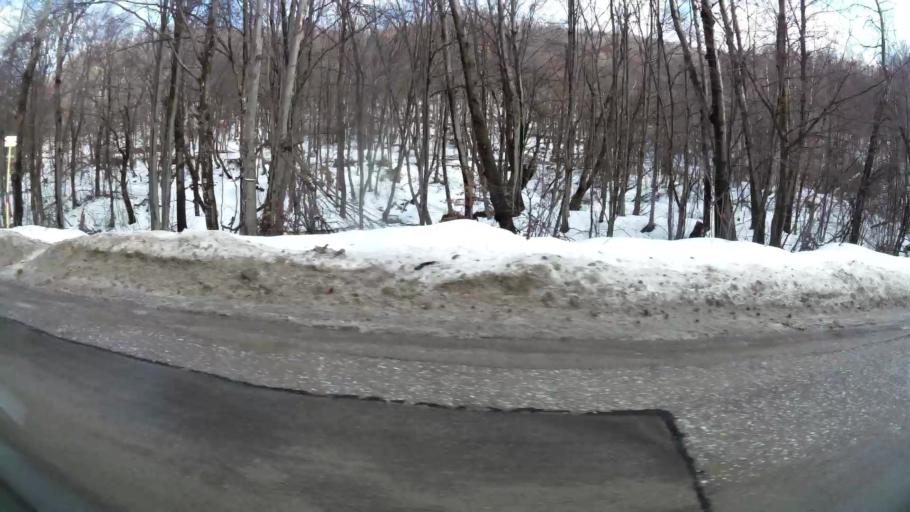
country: BG
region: Sofia-Capital
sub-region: Stolichna Obshtina
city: Sofia
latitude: 42.6320
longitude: 23.2252
